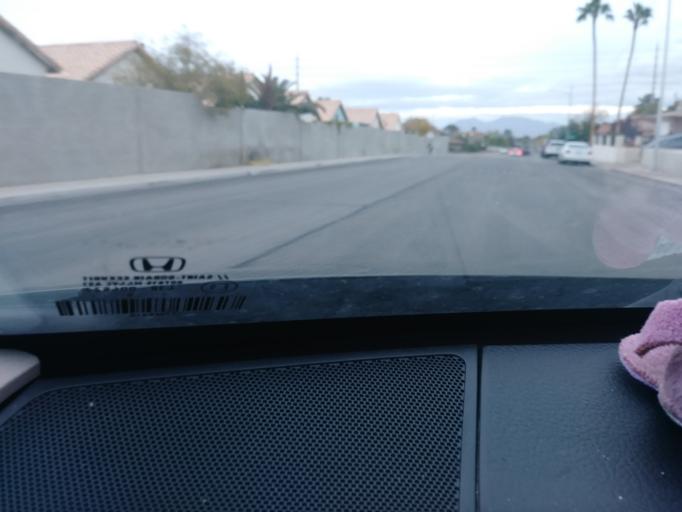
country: US
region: Nevada
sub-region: Clark County
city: Spring Valley
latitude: 36.1770
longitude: -115.2166
